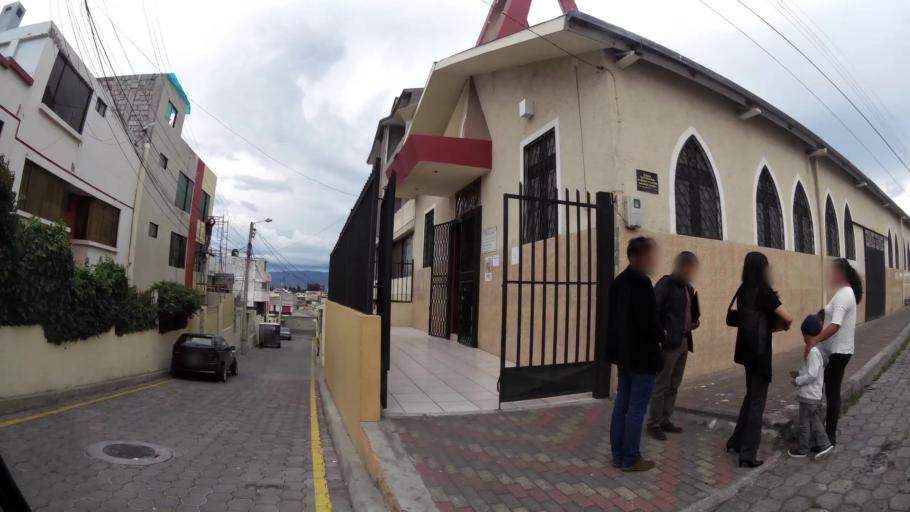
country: EC
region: Tungurahua
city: Ambato
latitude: -1.2595
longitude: -78.6326
